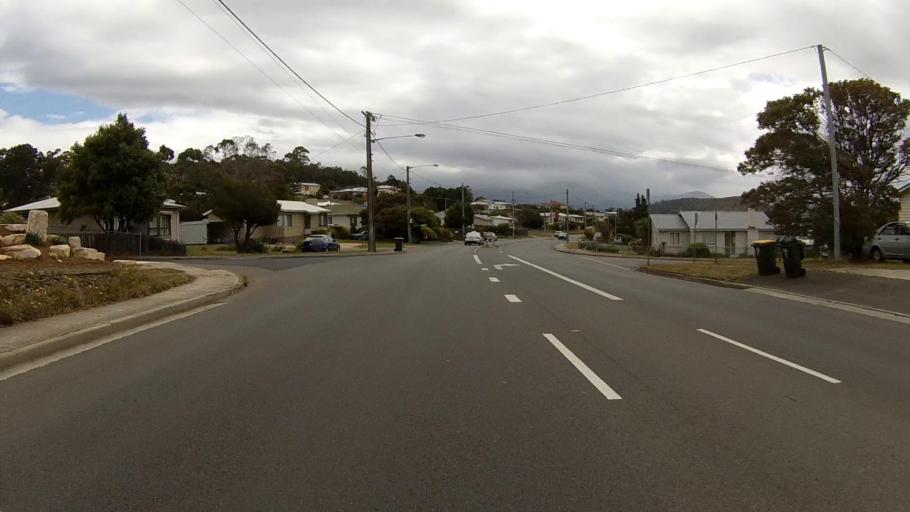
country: AU
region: Tasmania
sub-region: Clarence
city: Warrane
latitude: -42.8583
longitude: 147.3894
